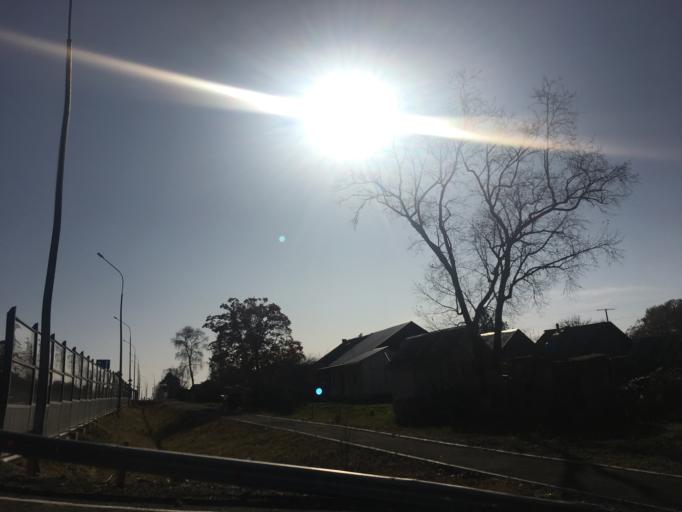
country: RU
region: Primorskiy
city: Dal'nerechensk
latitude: 45.8830
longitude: 133.7294
